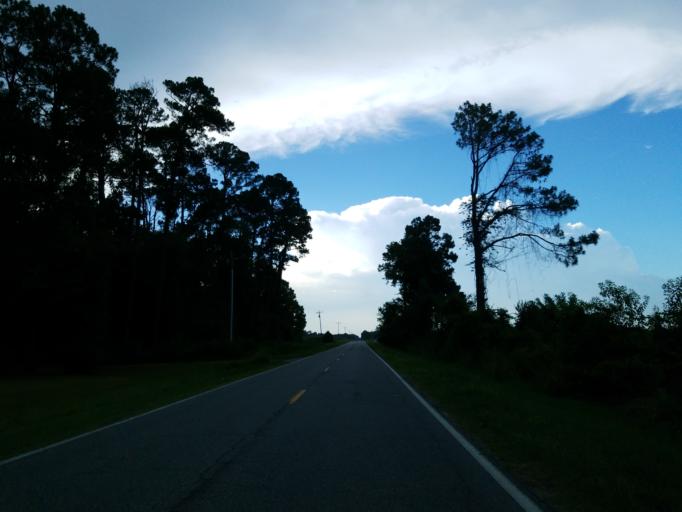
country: US
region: Georgia
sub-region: Tift County
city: Omega
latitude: 31.3051
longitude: -83.4728
